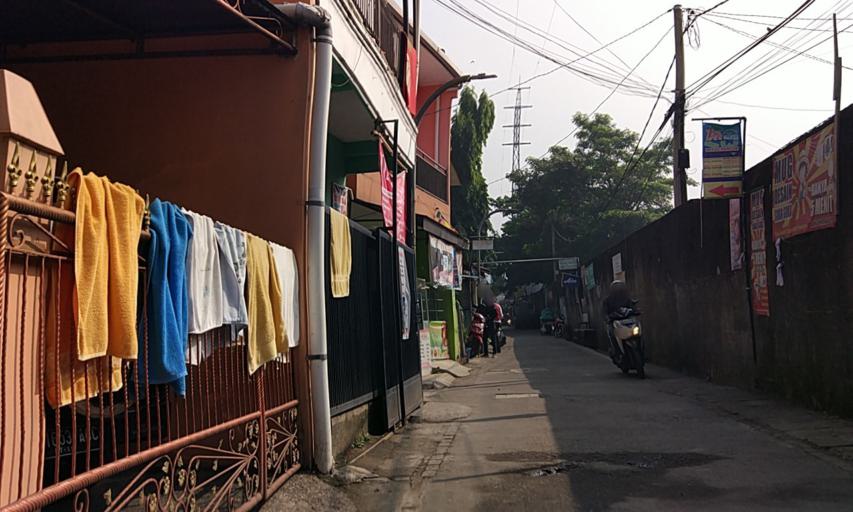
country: ID
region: West Java
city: Bandung
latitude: -6.9076
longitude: 107.6529
